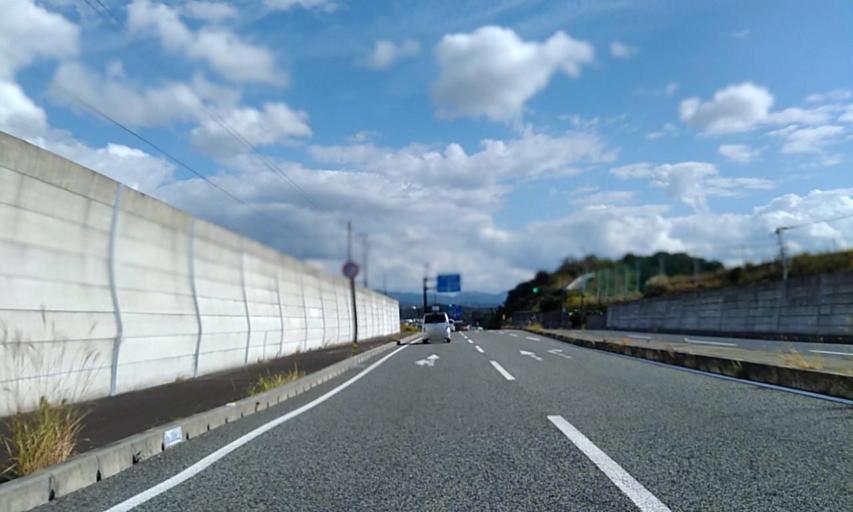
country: JP
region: Wakayama
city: Tanabe
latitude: 33.7476
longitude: 135.3648
